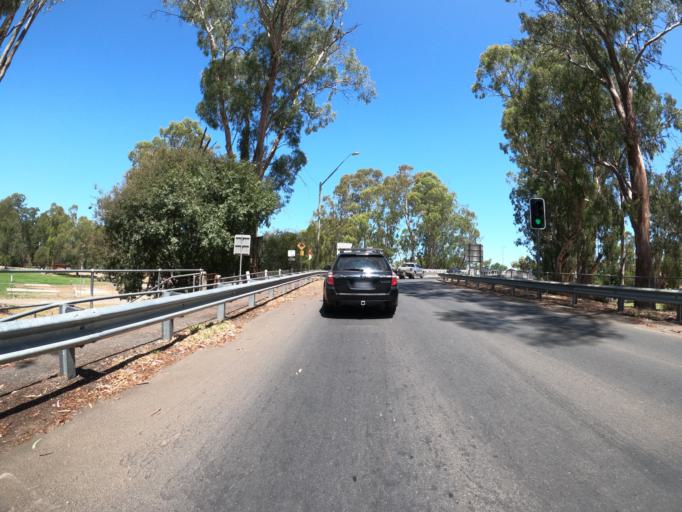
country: AU
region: New South Wales
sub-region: Corowa Shire
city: Corowa
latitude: -36.0056
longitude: 146.3953
